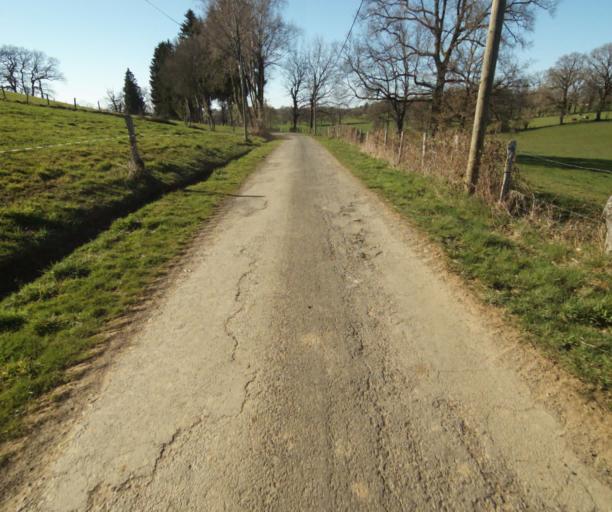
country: FR
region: Limousin
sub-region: Departement de la Correze
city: Seilhac
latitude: 45.3905
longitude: 1.6847
